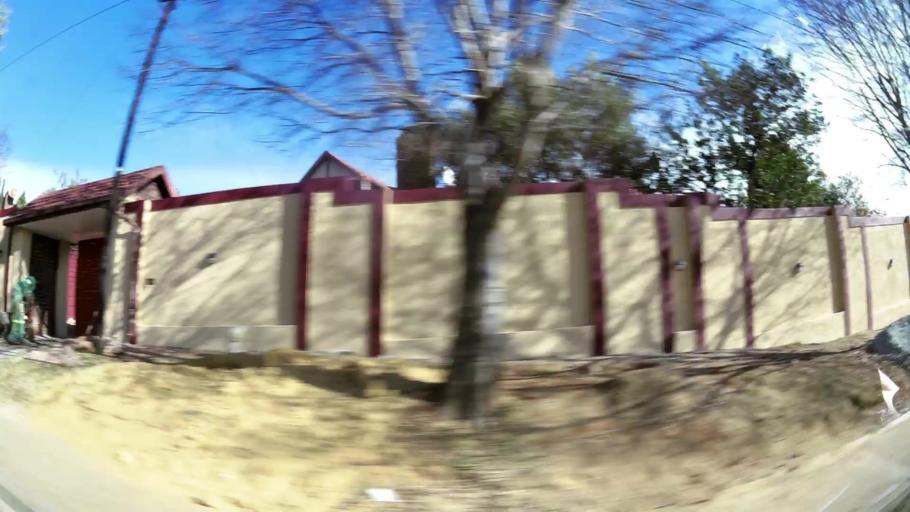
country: ZA
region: Gauteng
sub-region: City of Johannesburg Metropolitan Municipality
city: Roodepoort
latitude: -26.1212
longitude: 27.8499
